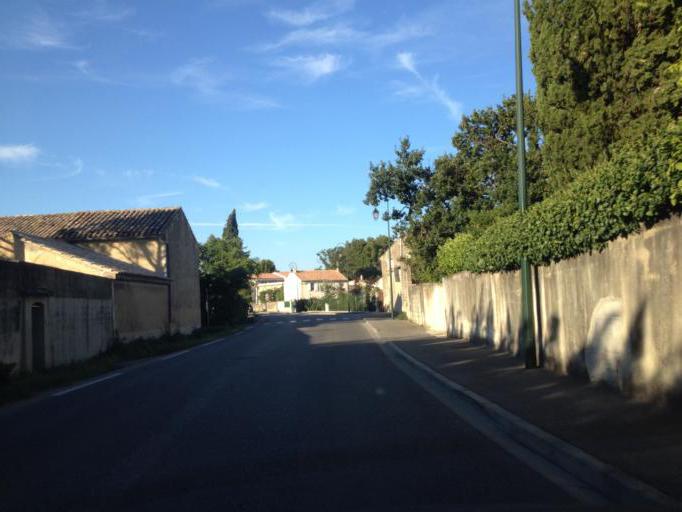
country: FR
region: Provence-Alpes-Cote d'Azur
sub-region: Departement du Vaucluse
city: Camaret-sur-Aigues
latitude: 44.1610
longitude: 4.8687
